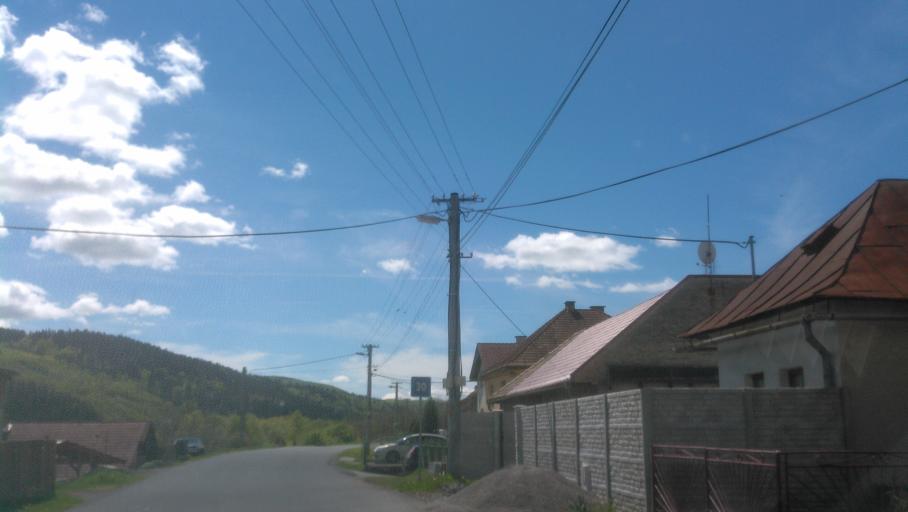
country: SK
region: Banskobystricky
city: Hrochot,Slovakia
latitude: 48.8124
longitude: 19.4112
